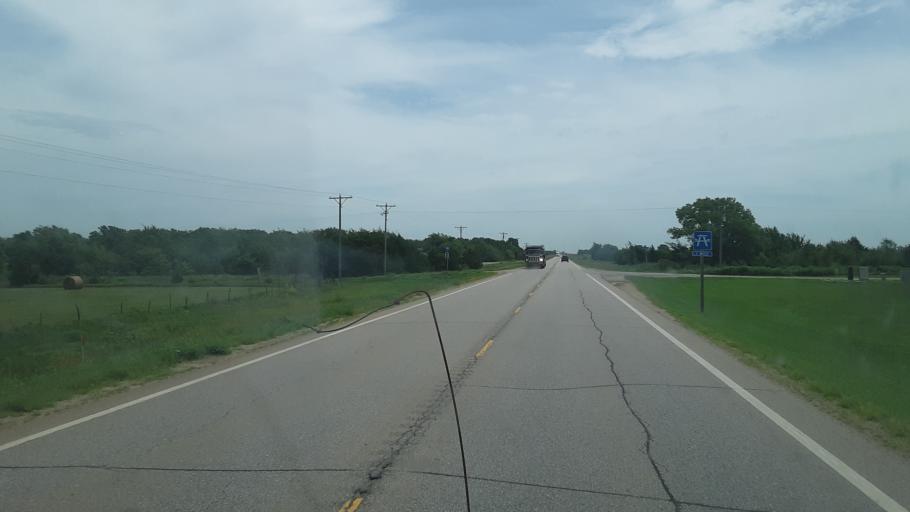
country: US
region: Kansas
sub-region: Butler County
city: El Dorado
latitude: 37.8103
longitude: -96.6809
